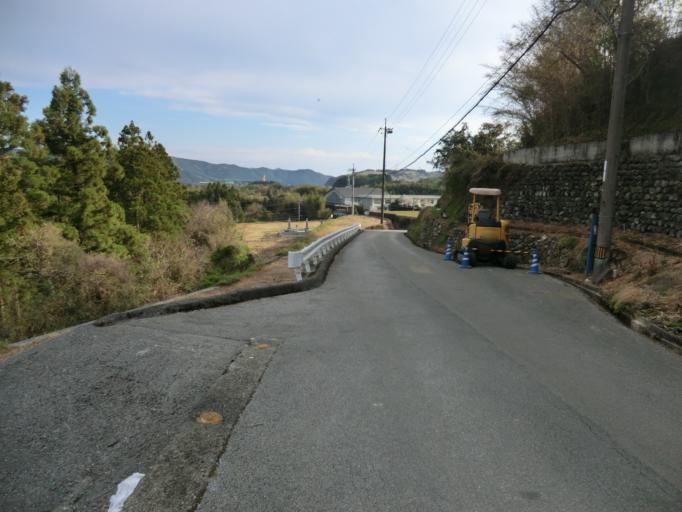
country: JP
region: Kochi
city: Kochi-shi
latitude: 33.6405
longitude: 133.7193
